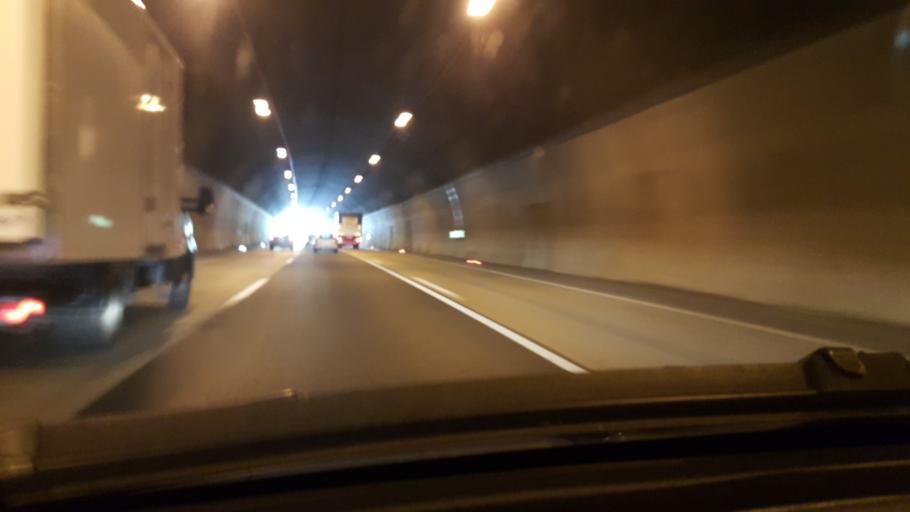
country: SI
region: Skofljica
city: Lavrica
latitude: 46.0206
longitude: 14.5624
